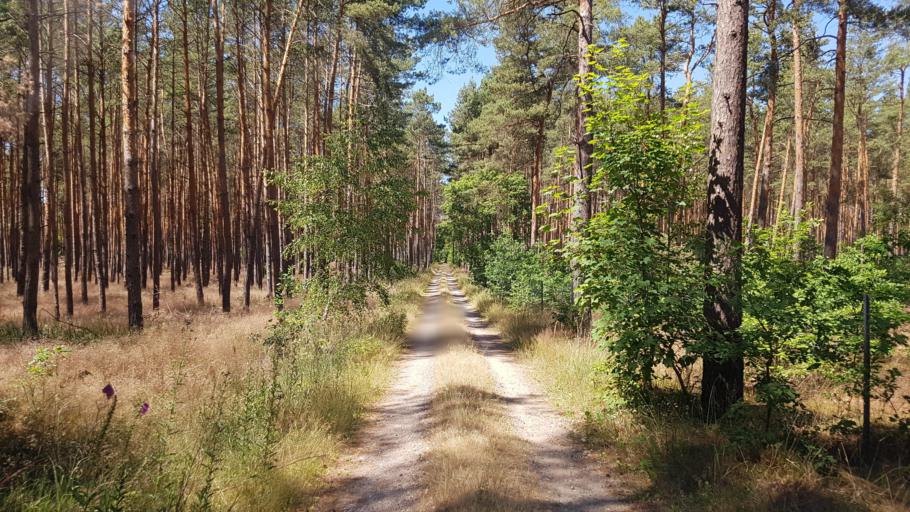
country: DE
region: Brandenburg
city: Treuenbrietzen
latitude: 52.0538
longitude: 12.8239
